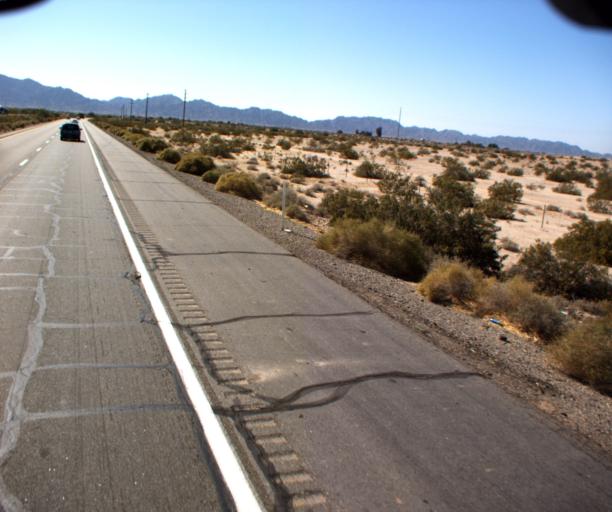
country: US
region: Arizona
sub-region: Yuma County
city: Wellton
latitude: 32.6507
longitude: -114.1903
